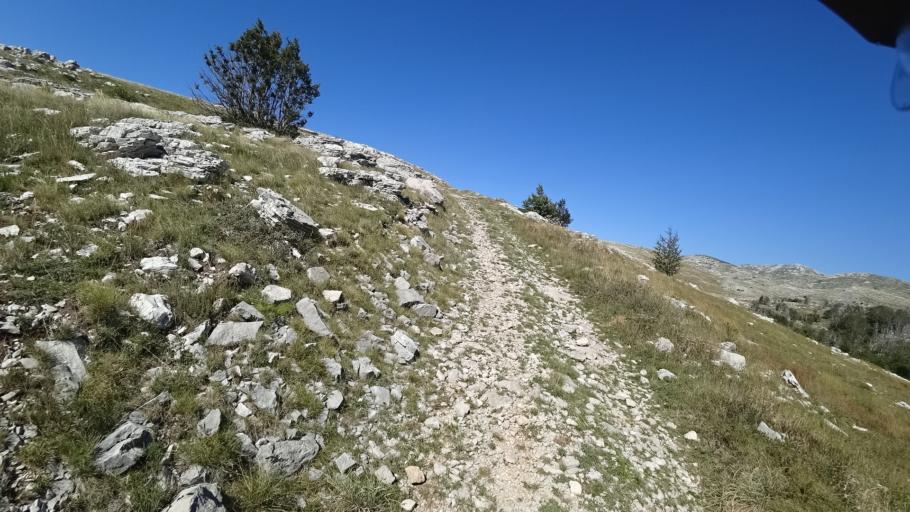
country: HR
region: Splitsko-Dalmatinska
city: Hrvace
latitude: 43.9152
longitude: 16.6087
